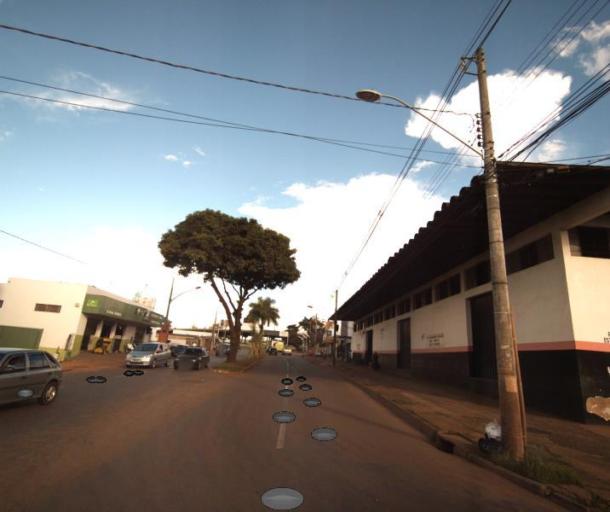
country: BR
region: Goias
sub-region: Anapolis
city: Anapolis
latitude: -16.3524
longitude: -48.9318
